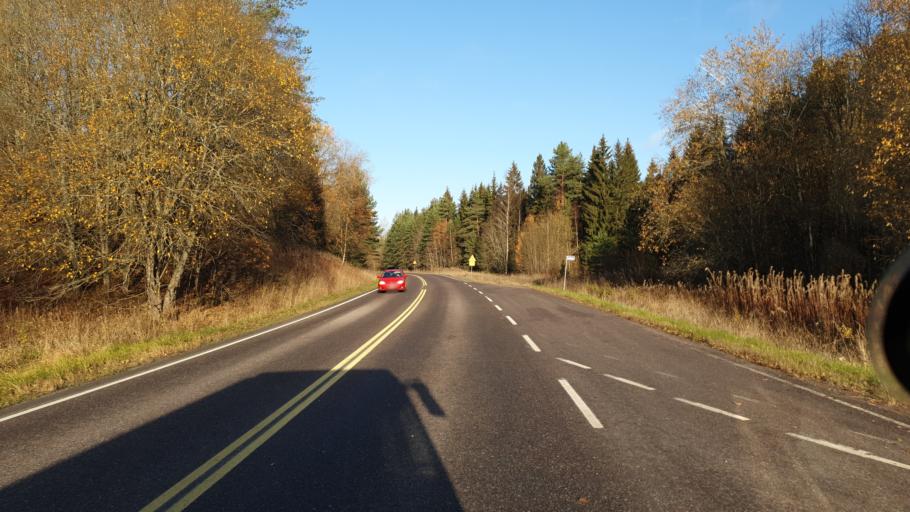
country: FI
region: Uusimaa
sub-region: Helsinki
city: Siuntio
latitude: 60.1910
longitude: 24.2019
